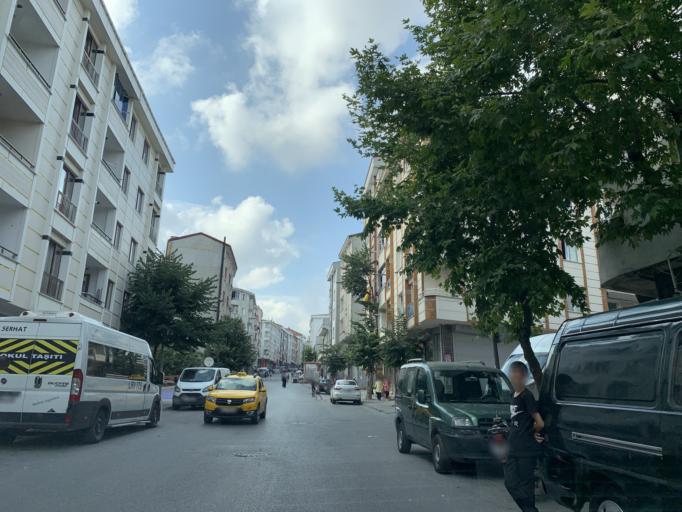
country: TR
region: Istanbul
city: Esenyurt
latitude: 41.0290
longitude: 28.6748
